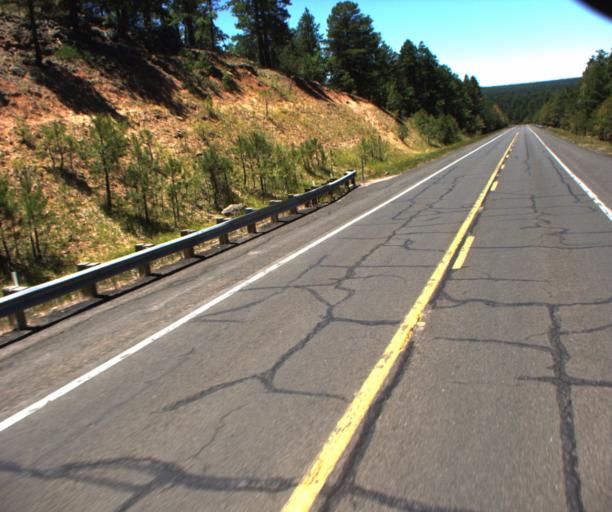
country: US
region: Arizona
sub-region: Gila County
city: Pine
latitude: 34.5525
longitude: -111.3002
